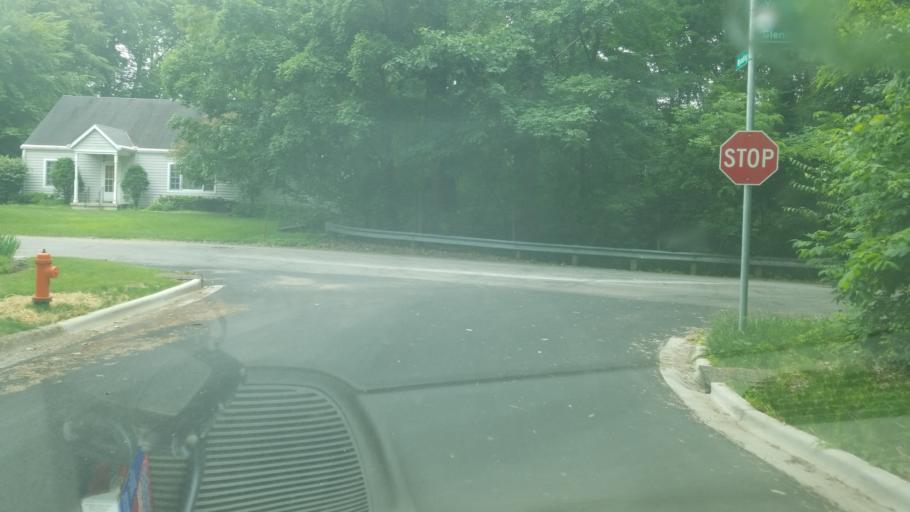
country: US
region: Ohio
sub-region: Franklin County
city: Worthington
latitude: 40.0444
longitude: -83.0032
